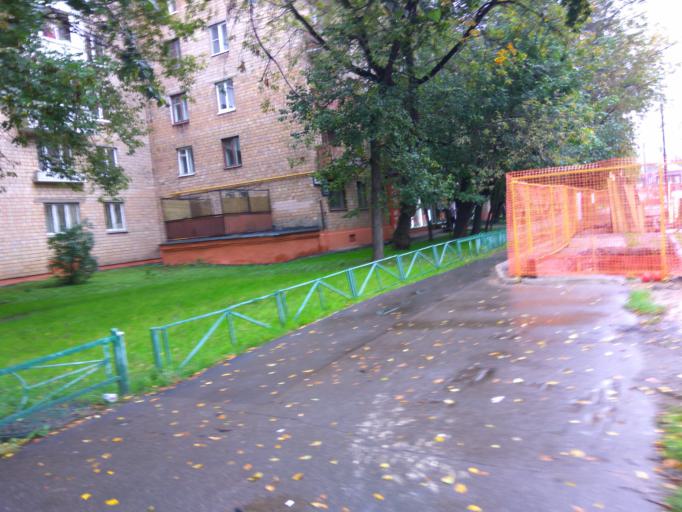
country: RU
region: Moskovskaya
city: Bogorodskoye
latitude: 55.7868
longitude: 37.7388
